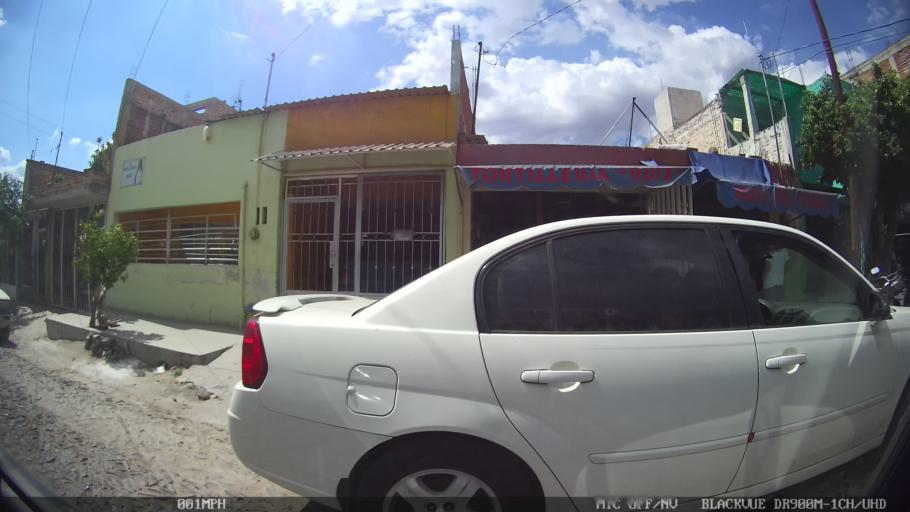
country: MX
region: Jalisco
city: Tlaquepaque
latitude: 20.6873
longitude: -103.2645
